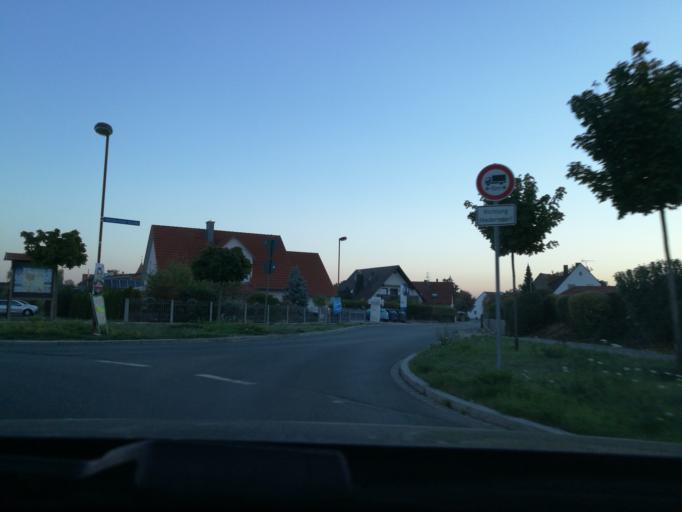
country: DE
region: Bavaria
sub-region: Regierungsbezirk Mittelfranken
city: Obermichelbach
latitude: 49.5287
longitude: 10.9076
